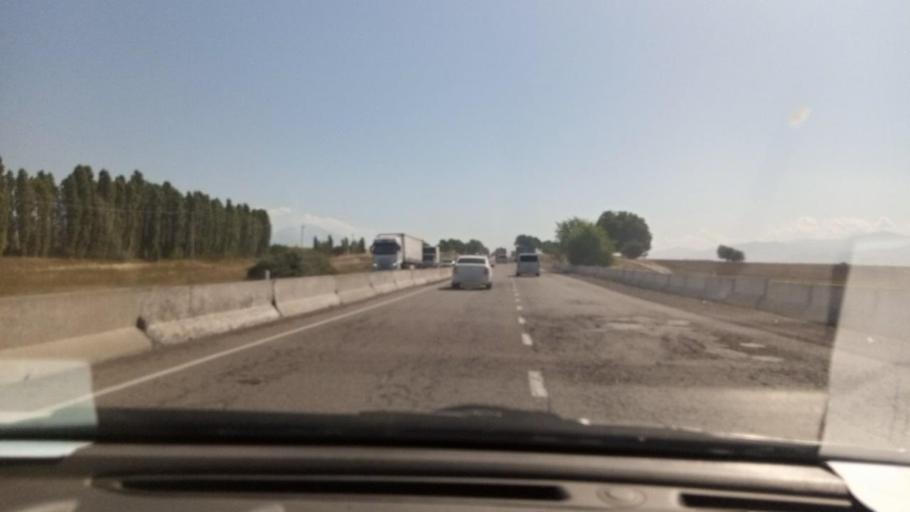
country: UZ
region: Toshkent
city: Angren
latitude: 40.9518
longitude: 69.9199
